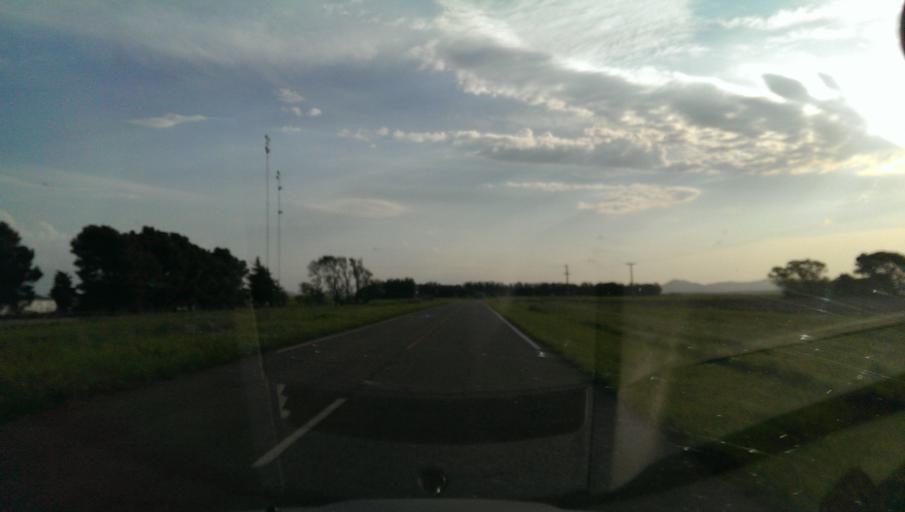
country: AR
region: Buenos Aires
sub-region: Partido de Coronel Suarez
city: Coronel Suarez
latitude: -37.8212
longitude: -61.8073
